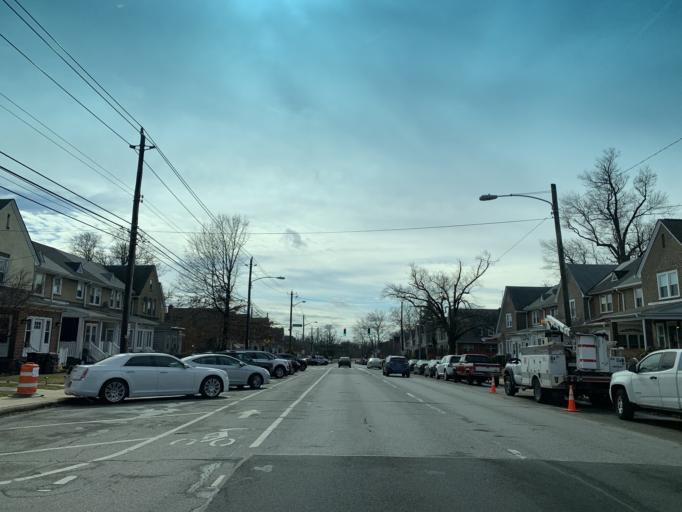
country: US
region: Delaware
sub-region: New Castle County
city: Elsmere
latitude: 39.7453
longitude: -75.5757
